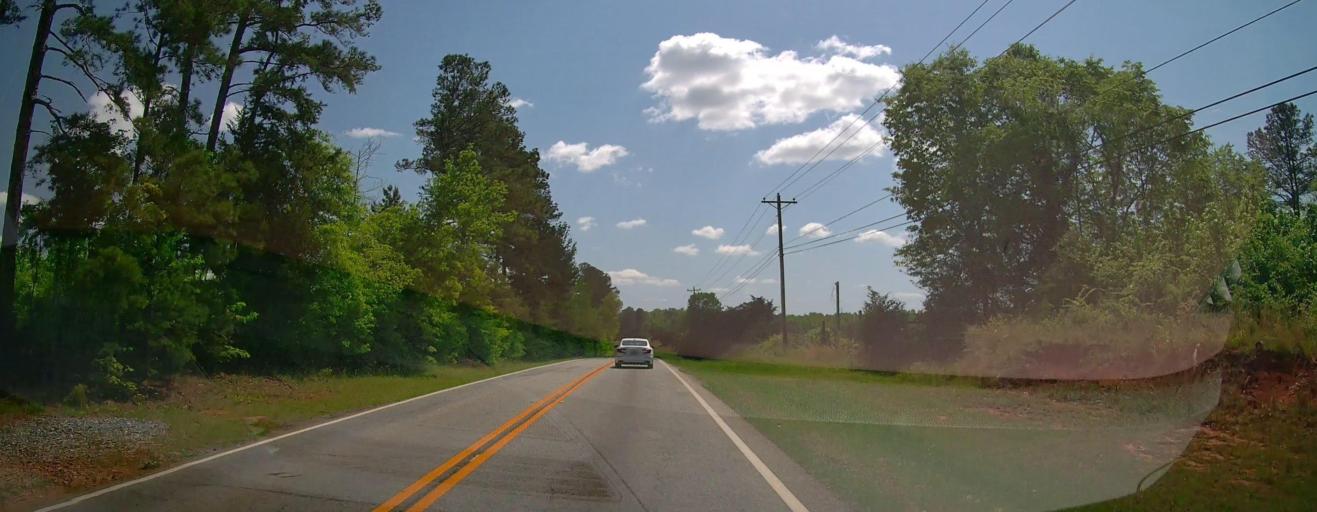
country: US
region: Georgia
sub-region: Putnam County
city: Eatonton
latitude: 33.3240
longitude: -83.2960
